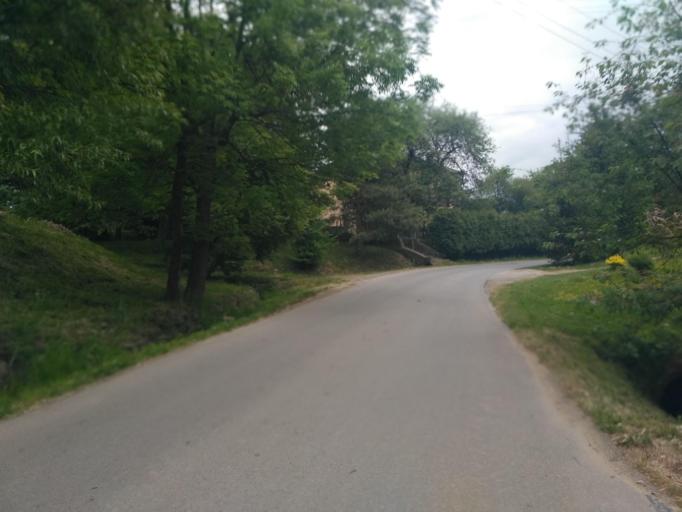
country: PL
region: Subcarpathian Voivodeship
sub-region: Powiat krosnienski
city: Jedlicze
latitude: 49.6880
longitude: 21.6440
